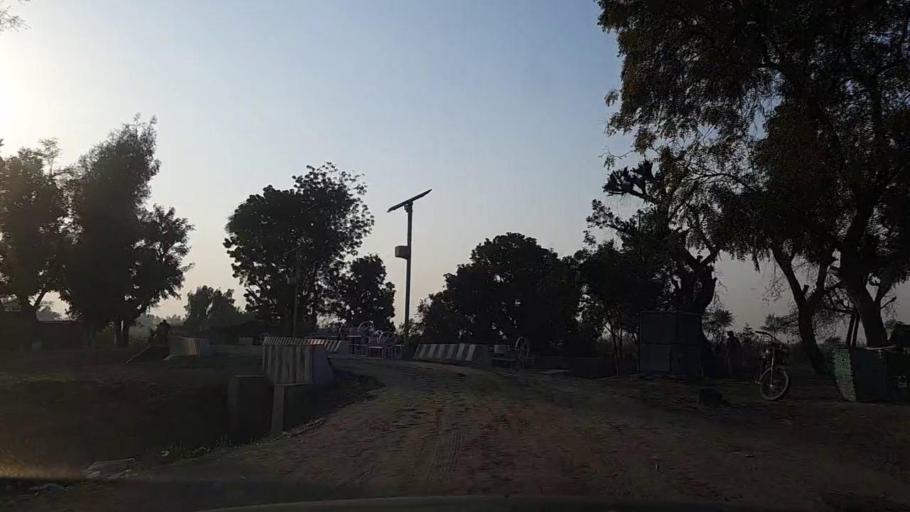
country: PK
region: Sindh
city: Daur
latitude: 26.4696
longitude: 68.3806
